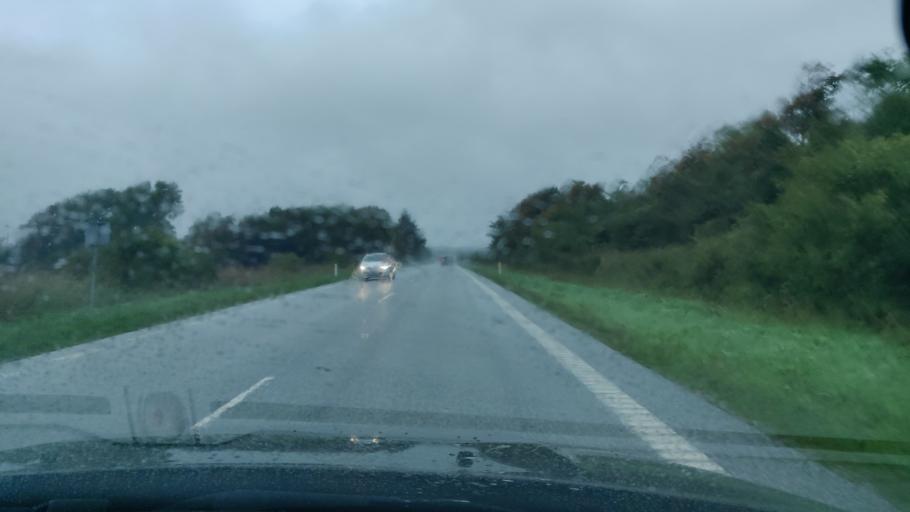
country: DK
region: North Denmark
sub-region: Thisted Kommune
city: Hurup
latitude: 56.8172
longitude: 8.4899
